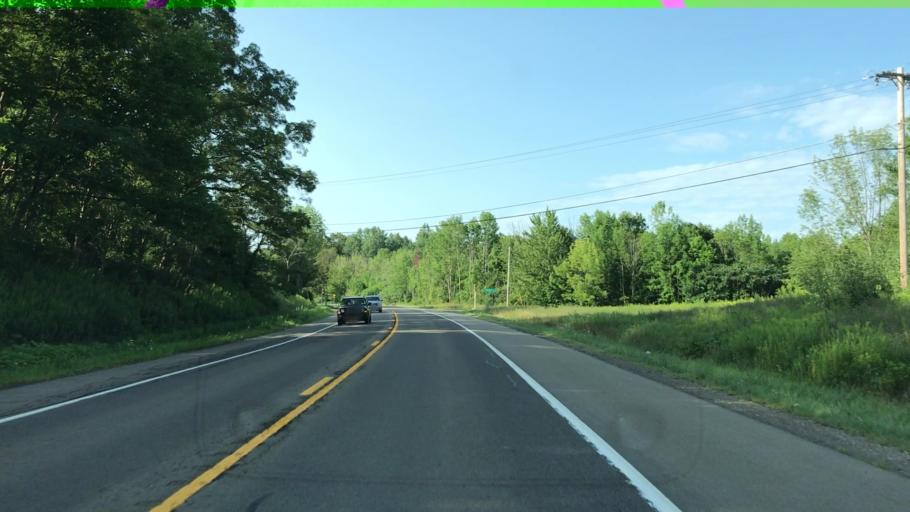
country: US
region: New York
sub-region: Chautauqua County
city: Fredonia
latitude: 42.3746
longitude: -79.3140
